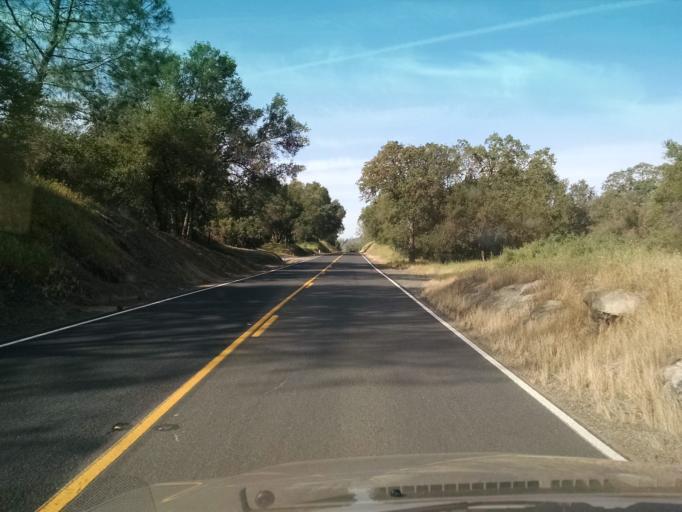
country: US
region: California
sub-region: Madera County
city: Yosemite Lakes
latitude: 37.1921
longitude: -119.7229
